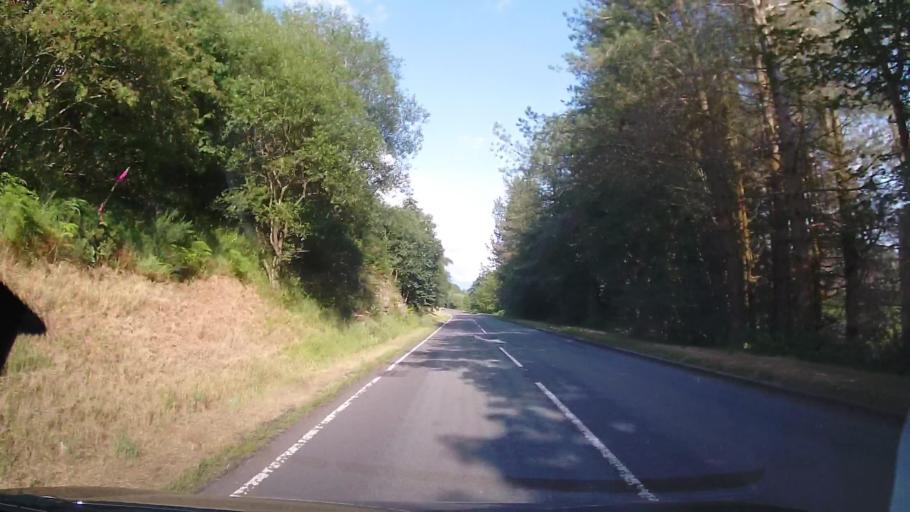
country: GB
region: Wales
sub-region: Gwynedd
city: Bala
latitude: 52.9550
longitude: -3.7095
